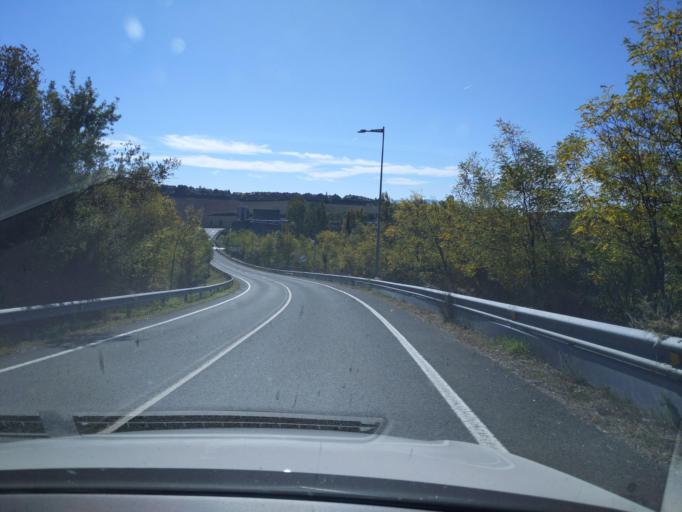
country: ES
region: Navarre
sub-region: Provincia de Navarra
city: Egues-Uharte
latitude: 42.8320
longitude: -1.5717
